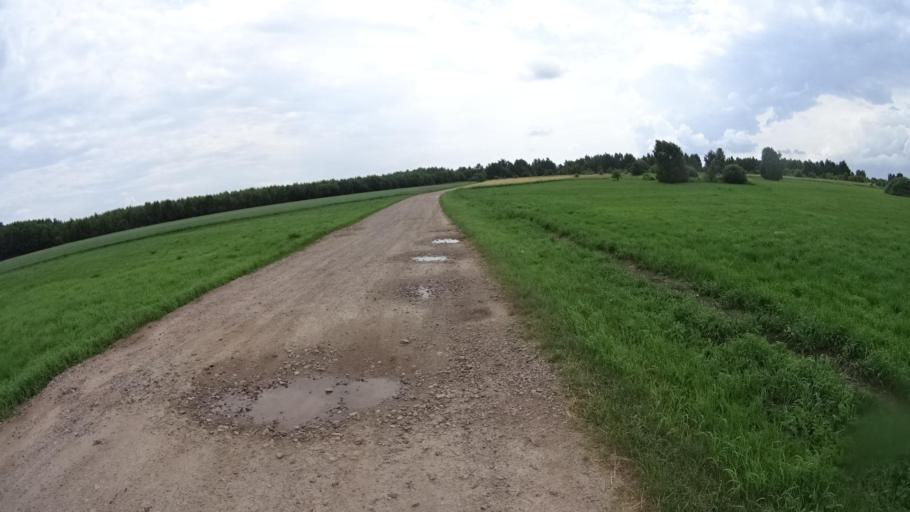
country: PL
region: Masovian Voivodeship
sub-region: Powiat piaseczynski
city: Tarczyn
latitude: 52.0219
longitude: 20.8173
